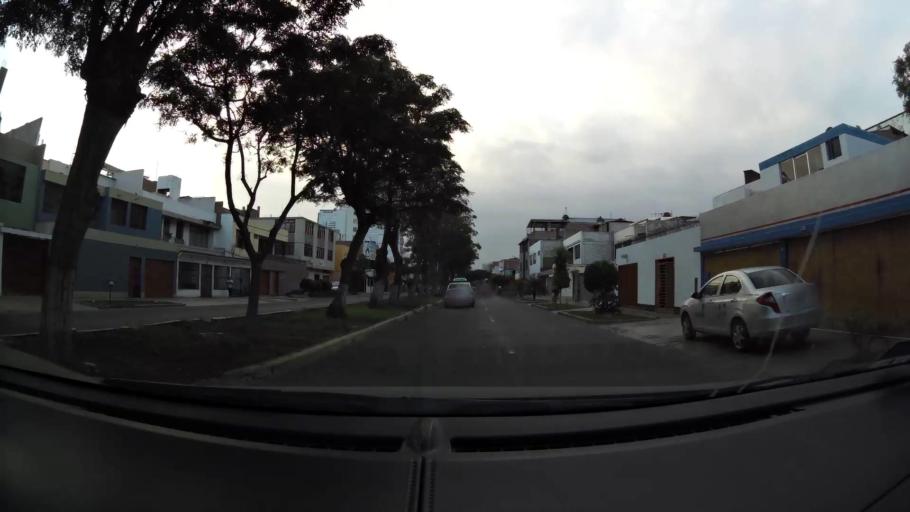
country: PE
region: La Libertad
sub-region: Provincia de Trujillo
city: Trujillo
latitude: -8.0998
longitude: -79.0322
